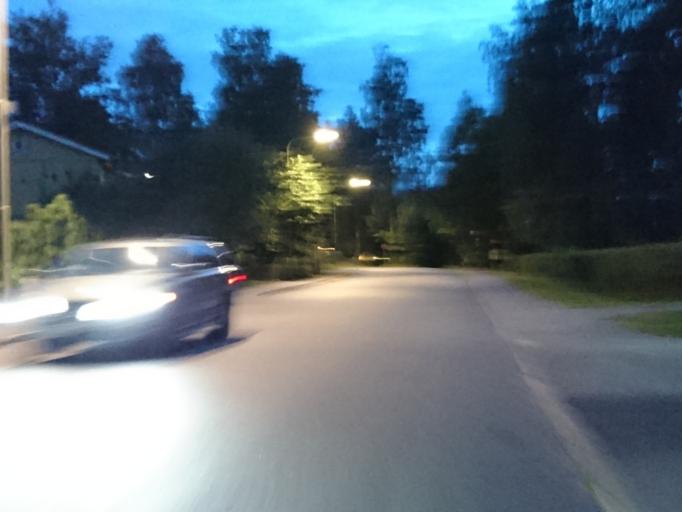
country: SE
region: Stockholm
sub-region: Huddinge Kommun
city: Segeltorp
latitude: 59.2785
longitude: 17.9574
